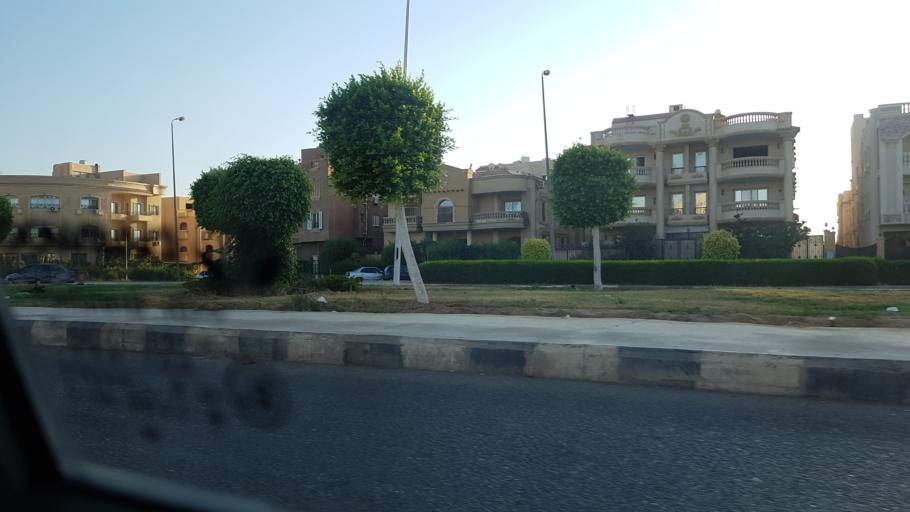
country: EG
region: Muhafazat al Qalyubiyah
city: Al Khankah
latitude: 30.0362
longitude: 31.4396
